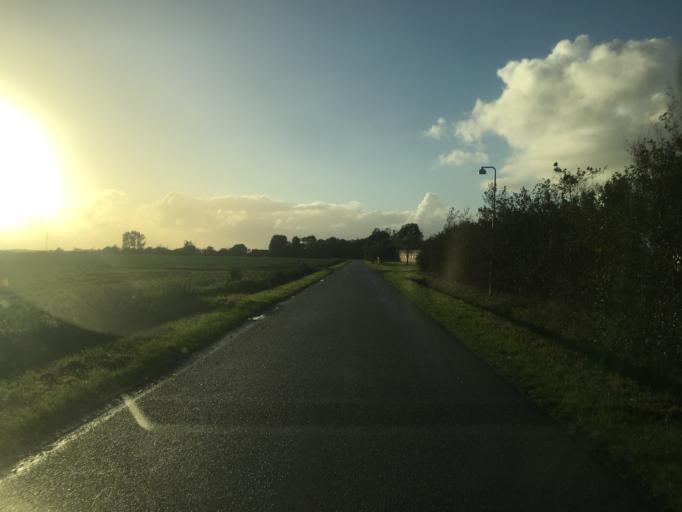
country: DE
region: Schleswig-Holstein
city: Aventoft
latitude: 54.9468
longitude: 8.7707
